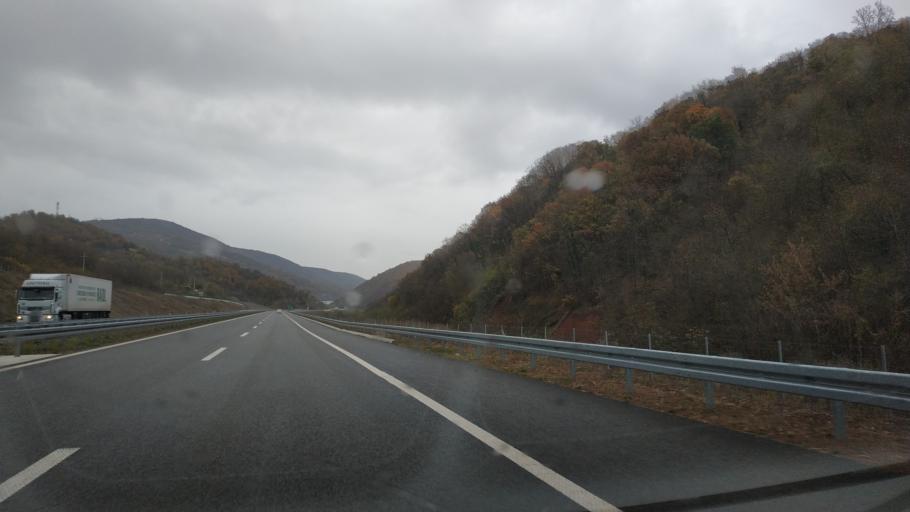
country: RS
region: Central Serbia
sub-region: Nisavski Okrug
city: Niska Banja
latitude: 43.2983
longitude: 22.0694
